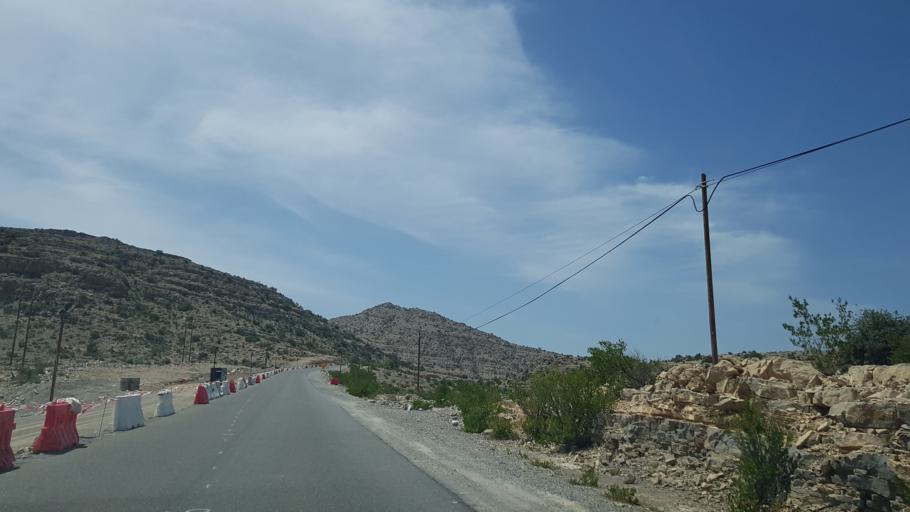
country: OM
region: Muhafazat ad Dakhiliyah
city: Izki
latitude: 23.1043
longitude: 57.6665
